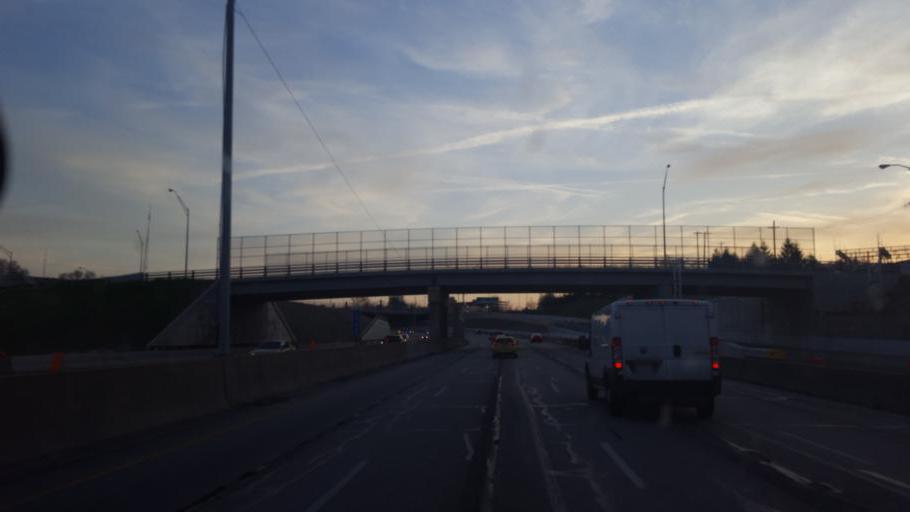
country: US
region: Kentucky
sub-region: Campbell County
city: Dayton
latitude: 39.1375
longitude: -84.4890
